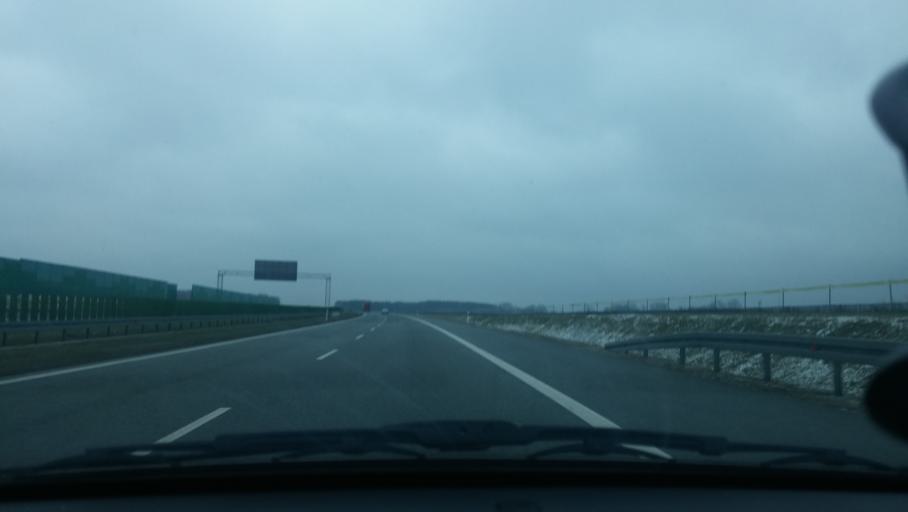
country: PL
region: Masovian Voivodeship
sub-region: Powiat minski
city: Jakubow
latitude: 52.2054
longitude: 21.6761
